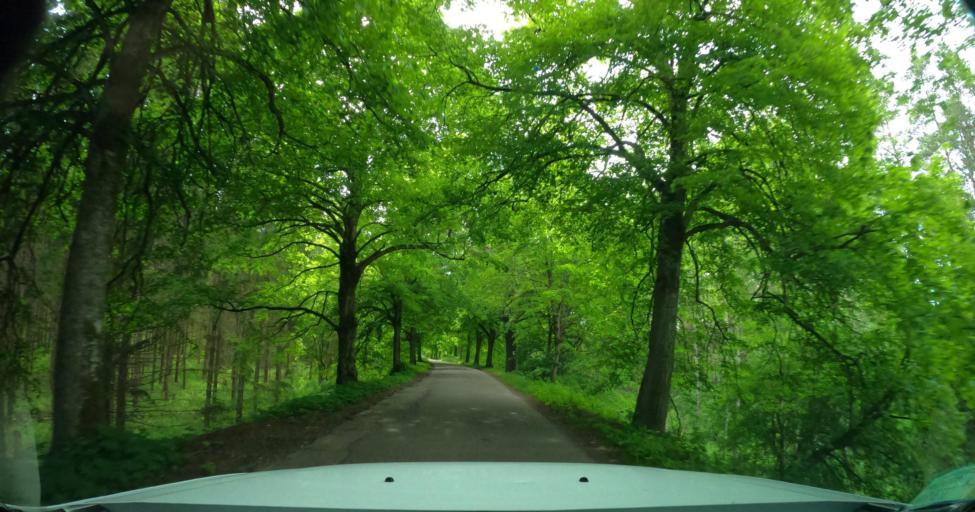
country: PL
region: Warmian-Masurian Voivodeship
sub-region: Powiat lidzbarski
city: Lubomino
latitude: 54.1047
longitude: 20.3535
